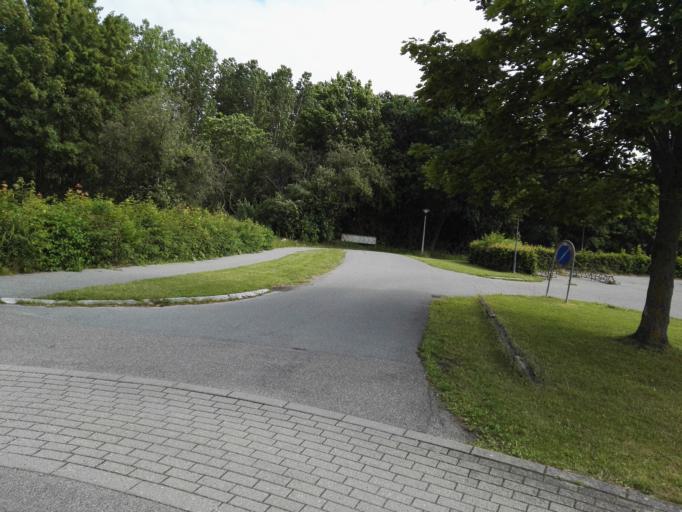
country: DK
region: Capital Region
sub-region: Egedal Kommune
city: Olstykke
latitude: 55.7838
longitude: 12.1453
